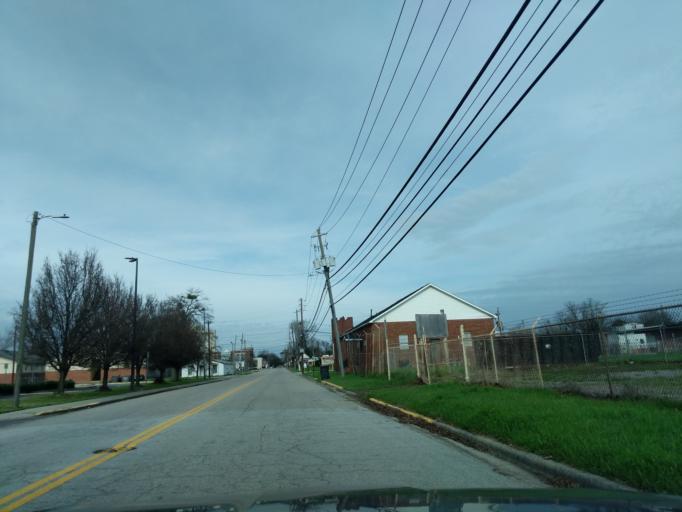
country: US
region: Georgia
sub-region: Richmond County
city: Augusta
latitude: 33.4619
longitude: -81.9612
